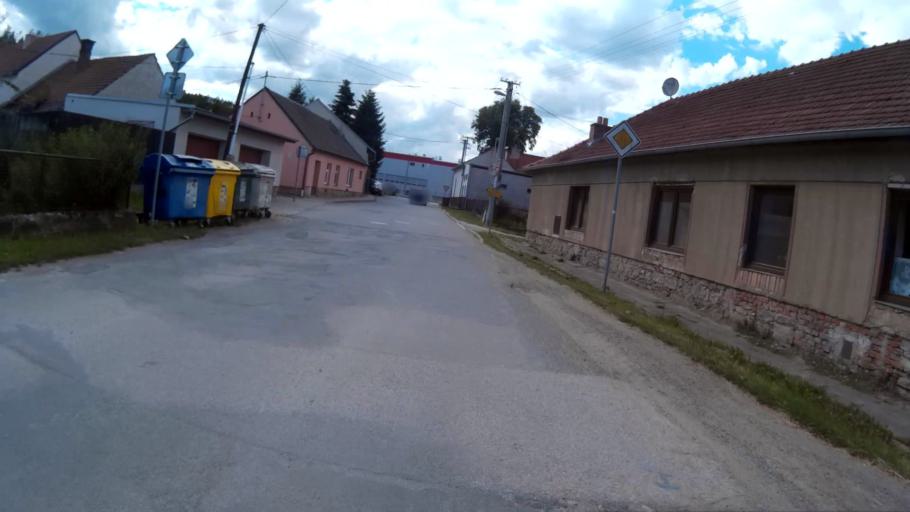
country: CZ
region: South Moravian
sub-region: Okres Brno-Venkov
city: Rosice
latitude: 49.1786
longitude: 16.3867
